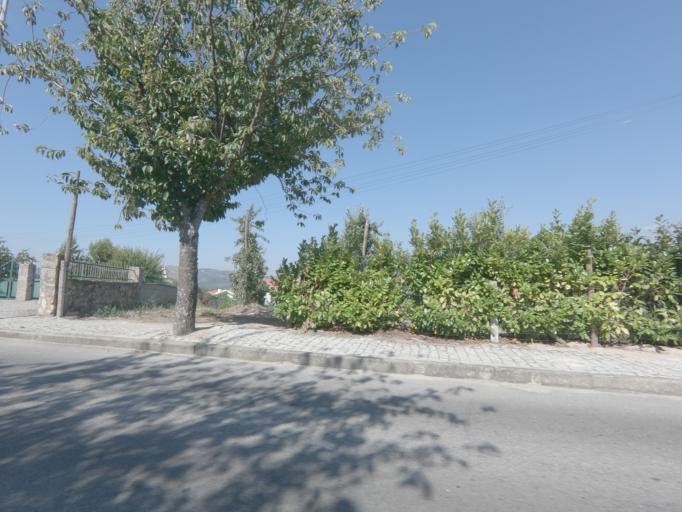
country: PT
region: Viseu
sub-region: Moimenta da Beira
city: Moimenta da Beira
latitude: 40.9802
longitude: -7.6177
